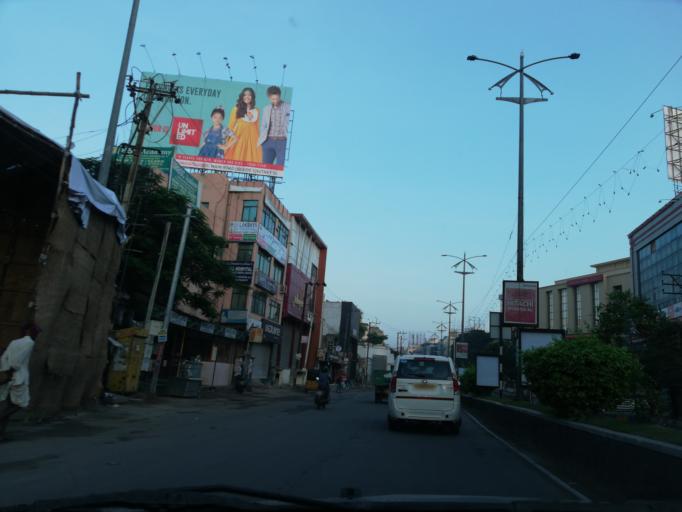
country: IN
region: Telangana
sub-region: Hyderabad
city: Hyderabad
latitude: 17.4024
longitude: 78.4835
